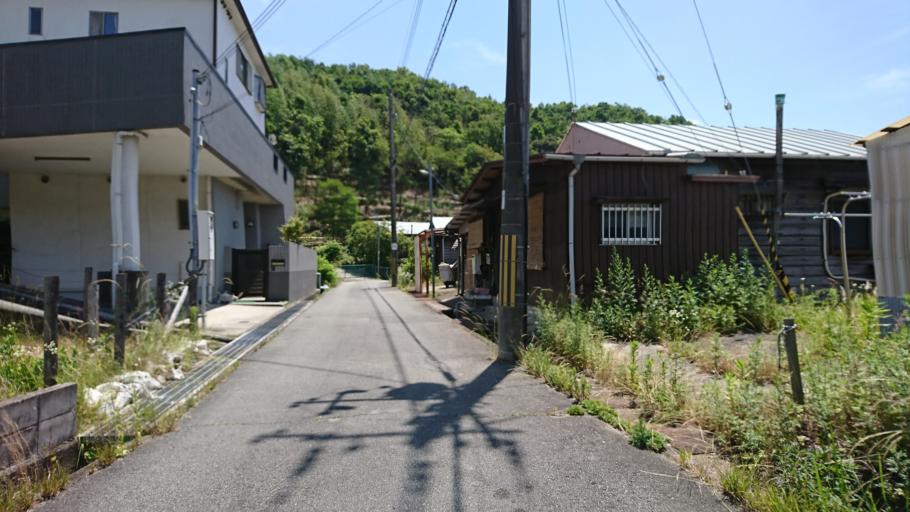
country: JP
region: Hyogo
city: Kakogawacho-honmachi
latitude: 34.8005
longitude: 134.7930
